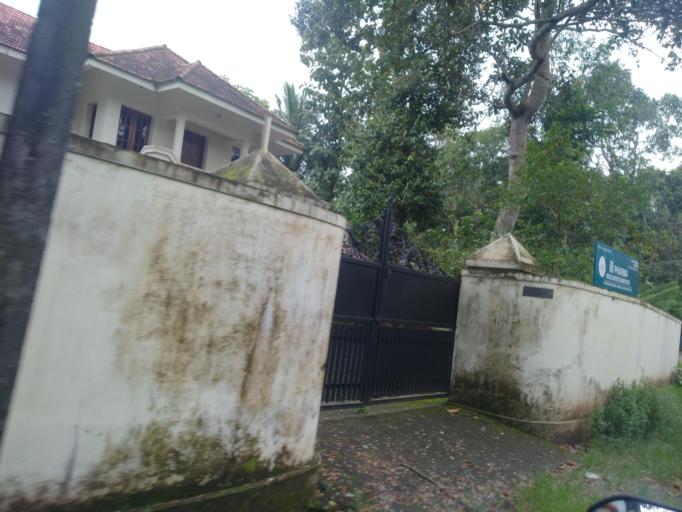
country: IN
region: Kerala
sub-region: Alappuzha
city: Shertallai
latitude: 9.6191
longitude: 76.3601
